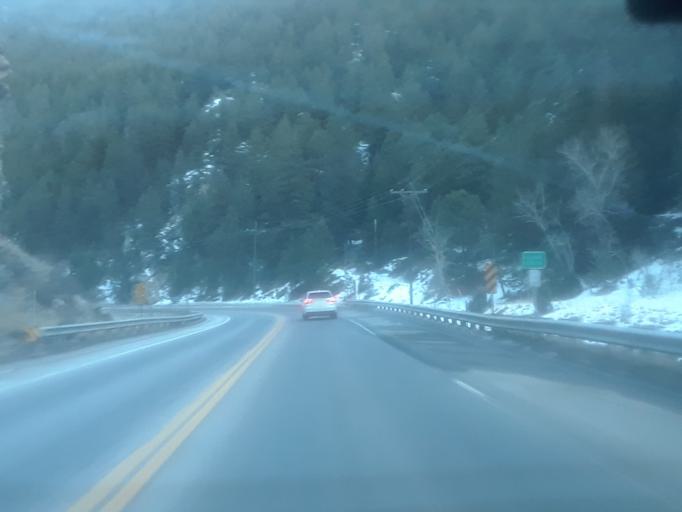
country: US
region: Colorado
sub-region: Clear Creek County
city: Idaho Springs
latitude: 39.7371
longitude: -105.4206
